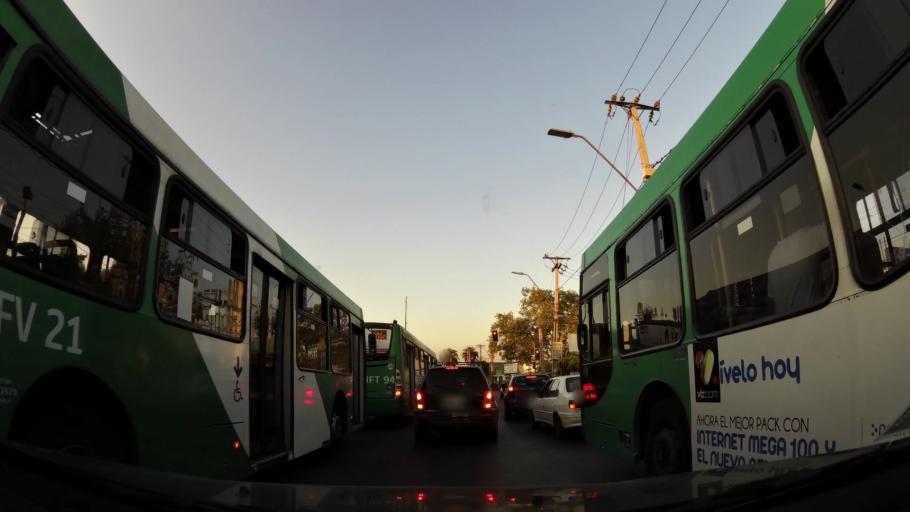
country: CL
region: Santiago Metropolitan
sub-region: Provincia de Santiago
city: La Pintana
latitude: -33.5431
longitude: -70.6662
